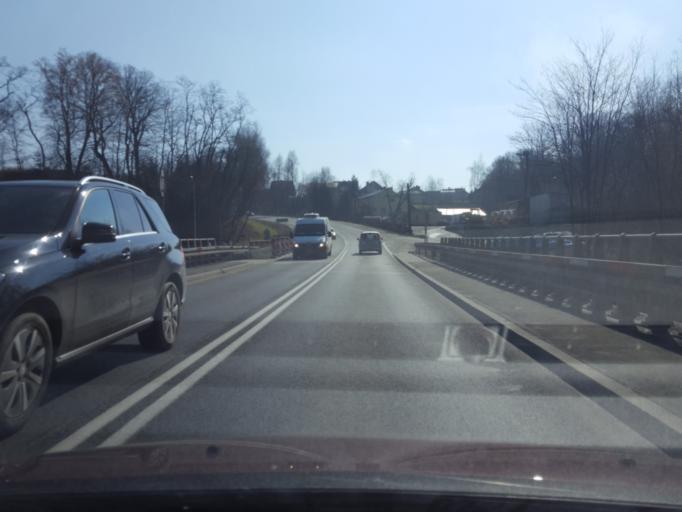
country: PL
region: Lesser Poland Voivodeship
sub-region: Powiat nowosadecki
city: Lososina Dolna
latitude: 49.7393
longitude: 20.6299
